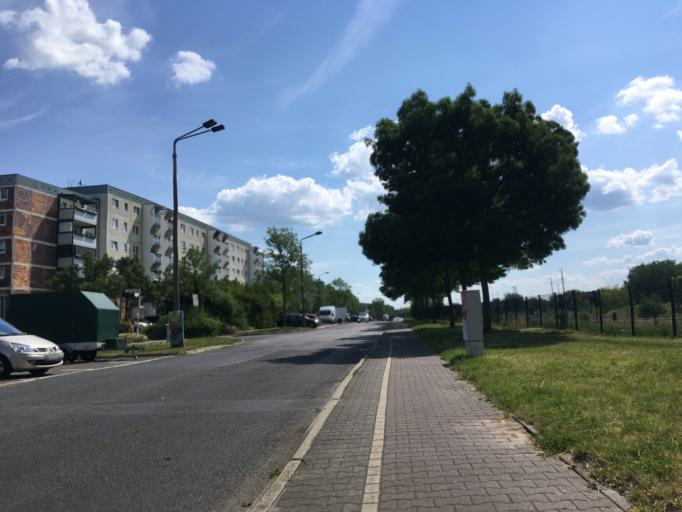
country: DE
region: Berlin
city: Hellersdorf
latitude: 52.5396
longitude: 13.6242
